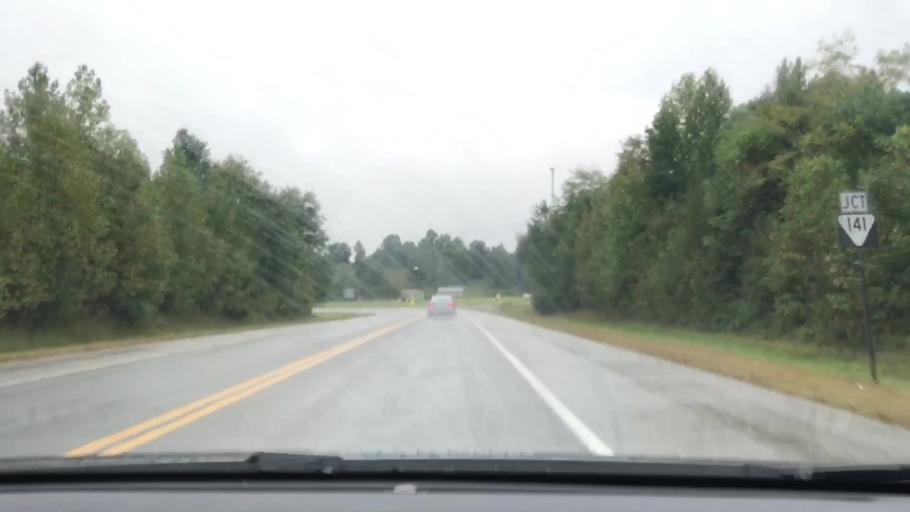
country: US
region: Tennessee
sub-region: Sumner County
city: Westmoreland
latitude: 36.5266
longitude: -86.1774
